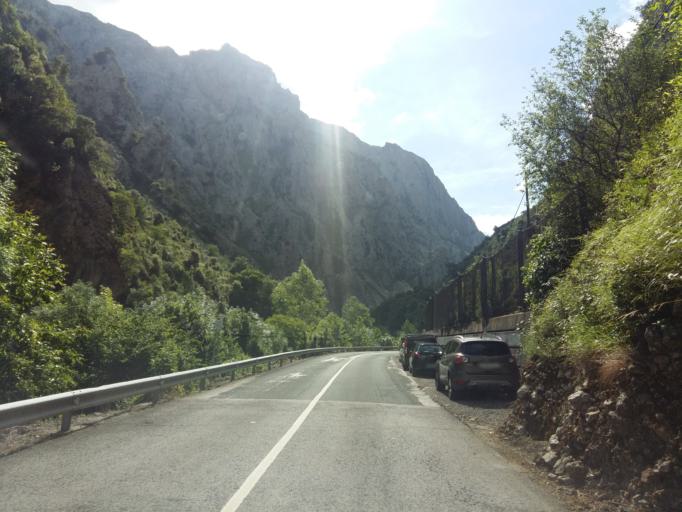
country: ES
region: Cantabria
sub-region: Provincia de Cantabria
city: Tresviso
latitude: 43.2659
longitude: -4.6298
